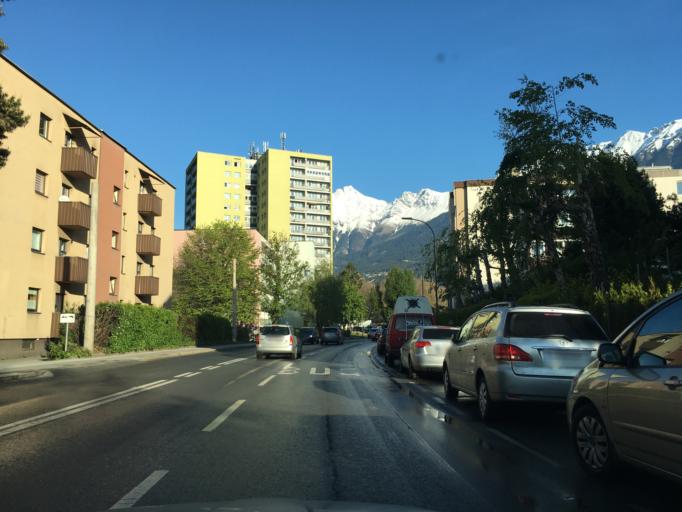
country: AT
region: Tyrol
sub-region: Politischer Bezirk Innsbruck Land
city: Ampass
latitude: 47.2745
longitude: 11.4343
